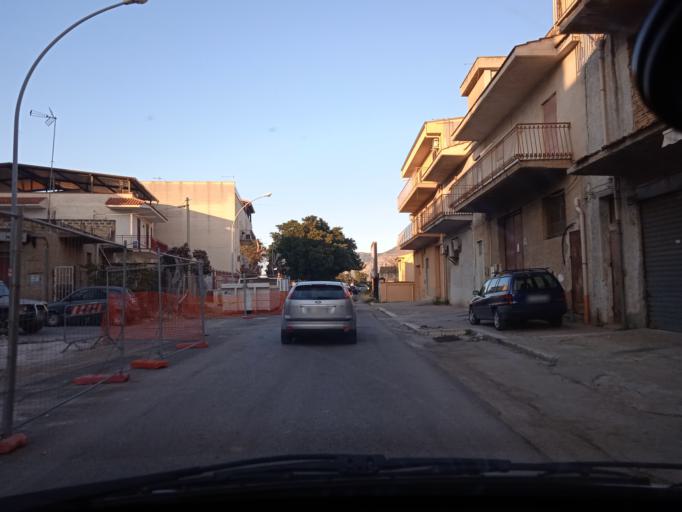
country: IT
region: Sicily
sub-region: Palermo
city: Ficarazzi
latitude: 38.0902
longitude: 13.4737
